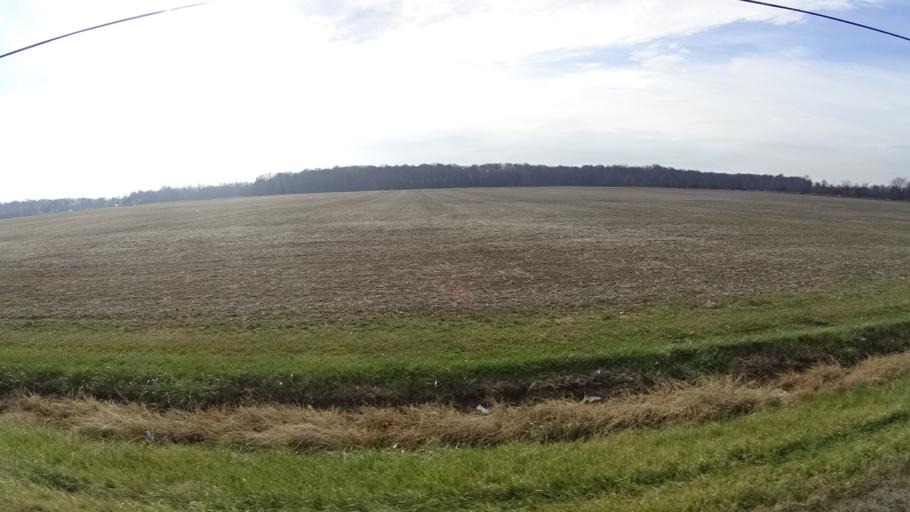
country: US
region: Ohio
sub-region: Lorain County
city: Eaton Estates
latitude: 41.2374
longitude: -81.9895
